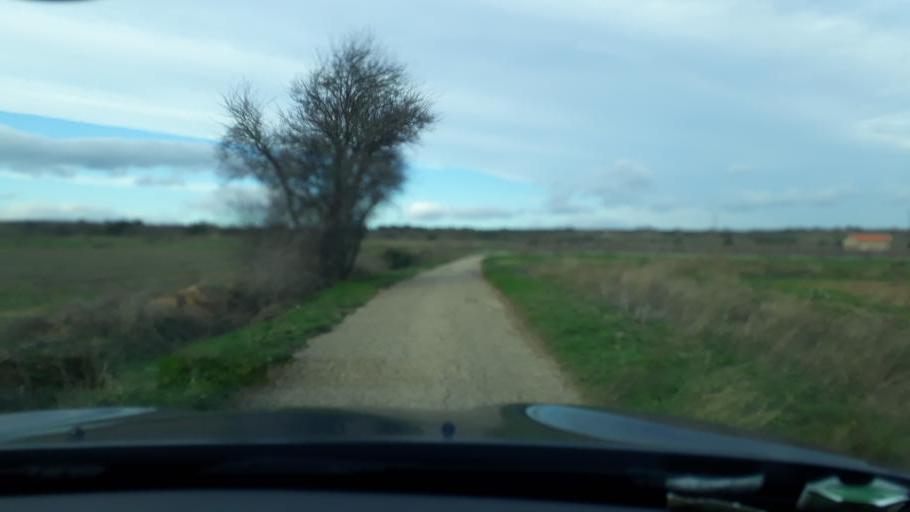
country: FR
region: Languedoc-Roussillon
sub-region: Departement de l'Herault
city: Florensac
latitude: 43.4040
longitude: 3.4599
